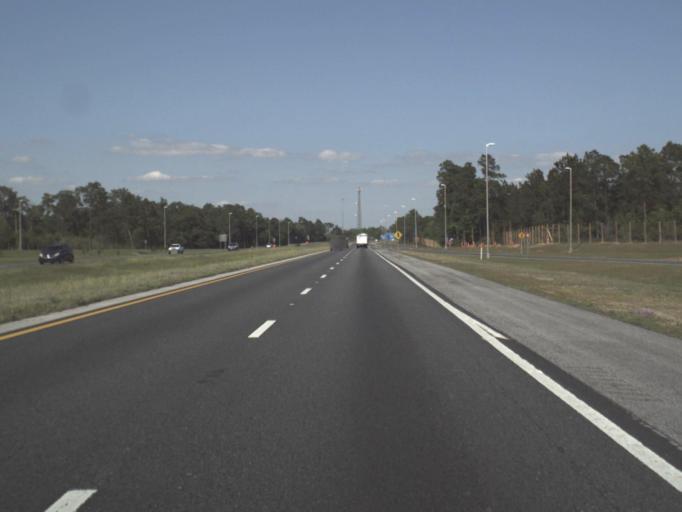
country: US
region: Florida
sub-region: Santa Rosa County
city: East Milton
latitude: 30.6113
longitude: -86.9775
